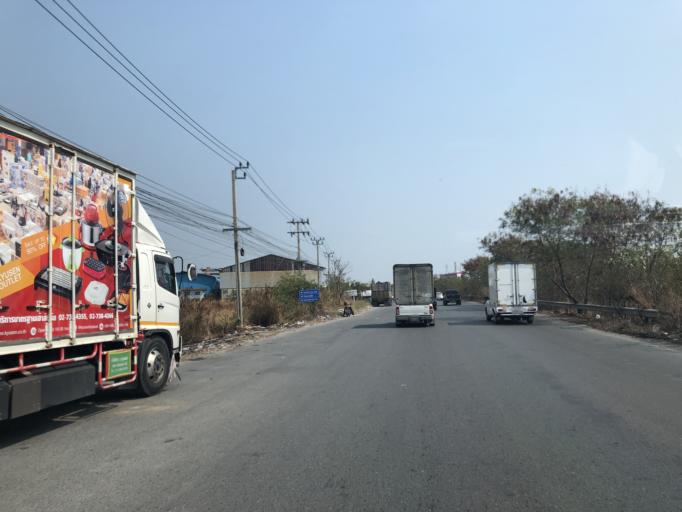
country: TH
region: Samut Prakan
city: Bang Bo District
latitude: 13.5890
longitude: 100.7602
